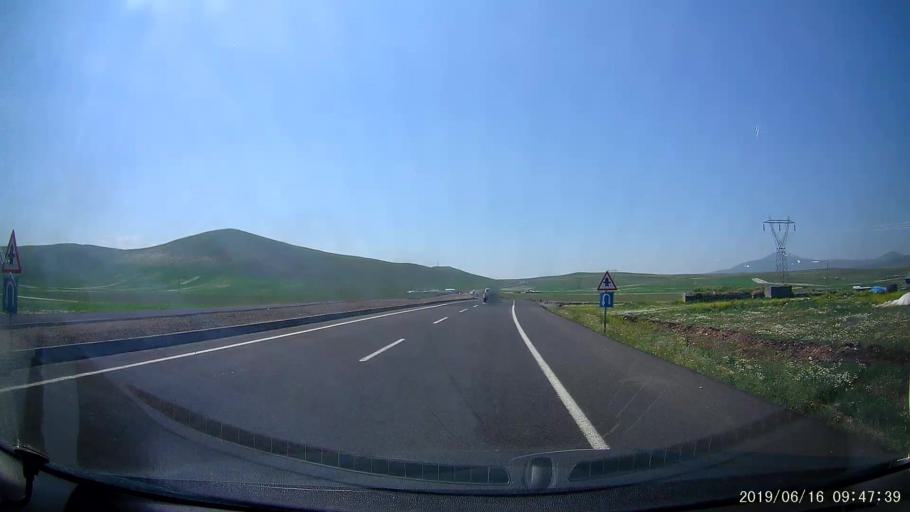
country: TR
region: Kars
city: Digor
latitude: 40.4435
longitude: 43.3464
